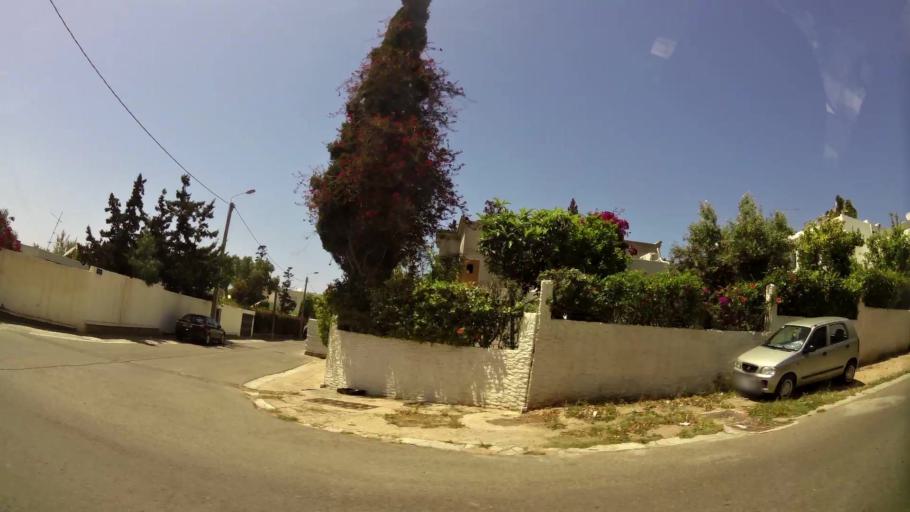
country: MA
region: Souss-Massa-Draa
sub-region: Agadir-Ida-ou-Tnan
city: Agadir
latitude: 30.4277
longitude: -9.5995
